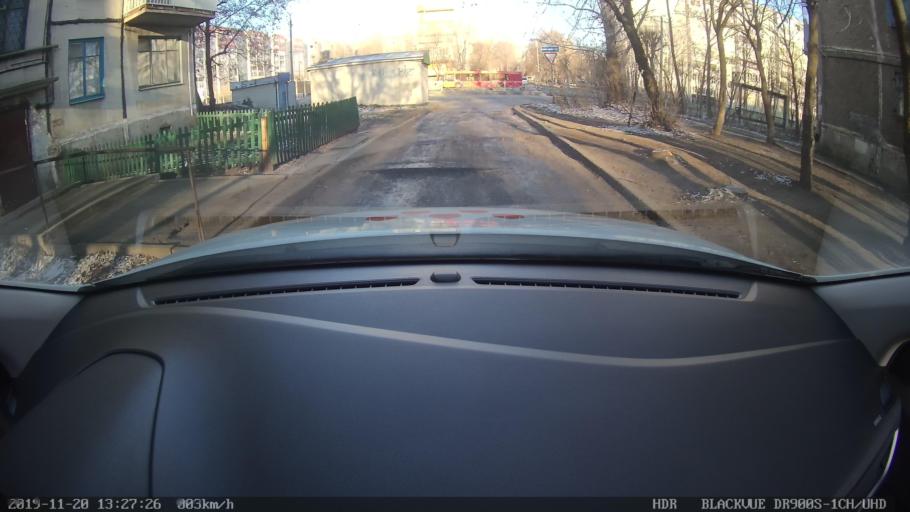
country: RU
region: Tatarstan
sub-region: Gorod Kazan'
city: Kazan
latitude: 55.8243
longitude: 49.0545
